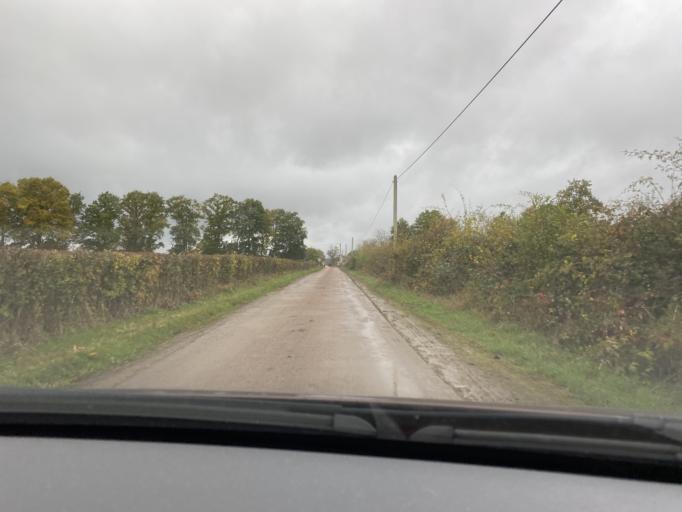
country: FR
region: Bourgogne
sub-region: Departement de la Cote-d'Or
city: Saulieu
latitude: 47.2807
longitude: 4.1957
